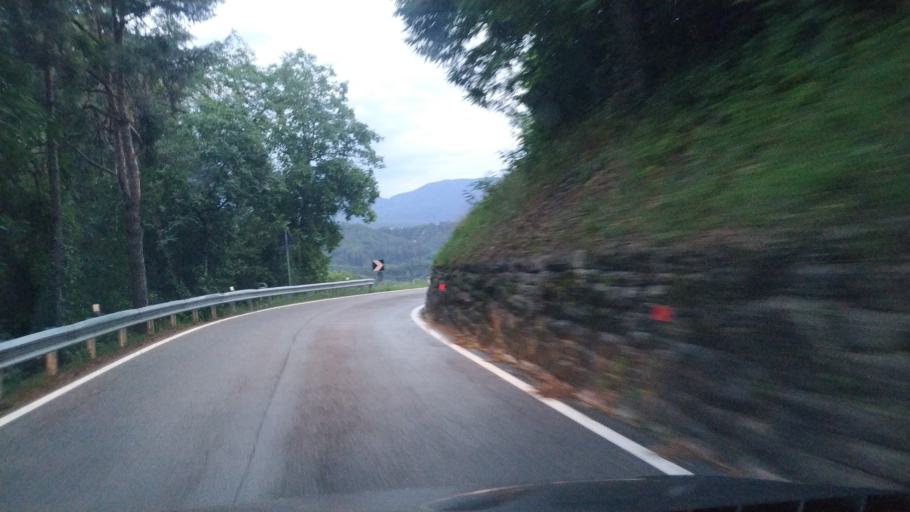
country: IT
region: Trentino-Alto Adige
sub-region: Provincia di Trento
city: Brez
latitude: 46.4407
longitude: 11.1109
